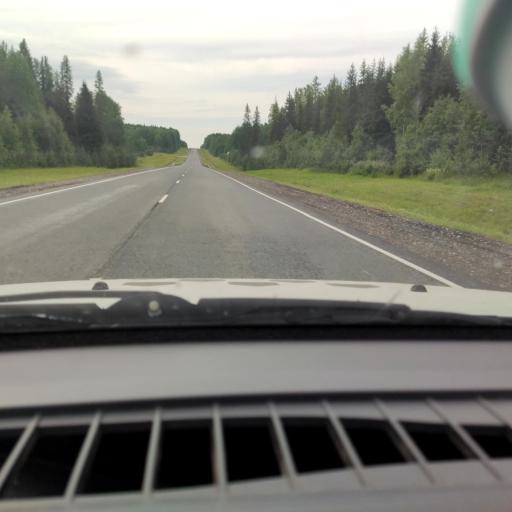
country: RU
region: Kirov
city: Kostino
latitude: 58.7970
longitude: 53.5983
